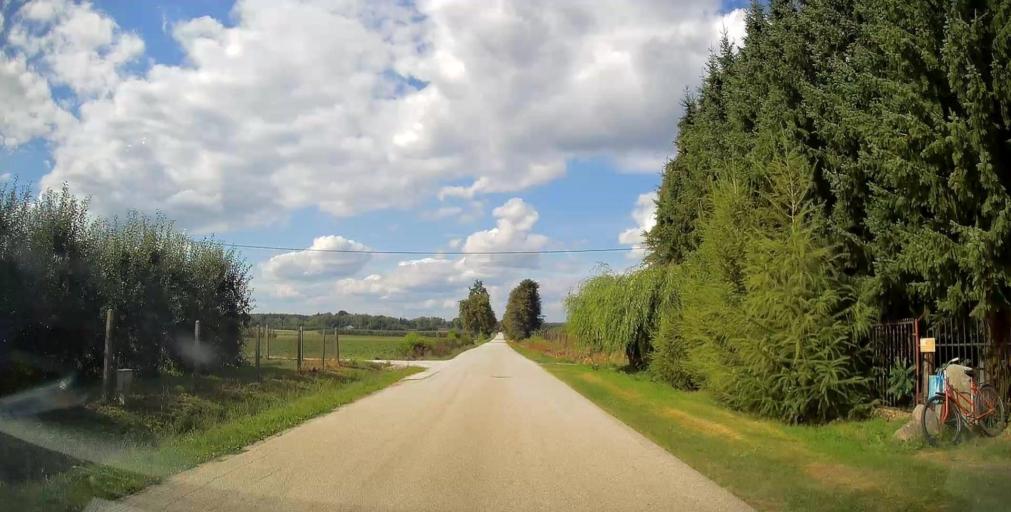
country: PL
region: Masovian Voivodeship
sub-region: Powiat grojecki
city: Goszczyn
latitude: 51.7055
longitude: 20.8949
